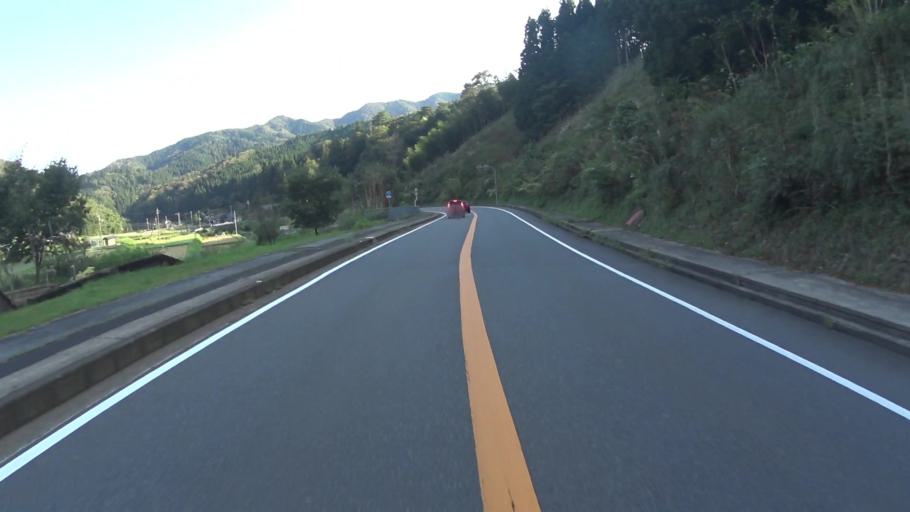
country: JP
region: Kyoto
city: Fukuchiyama
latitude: 35.4298
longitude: 135.0675
